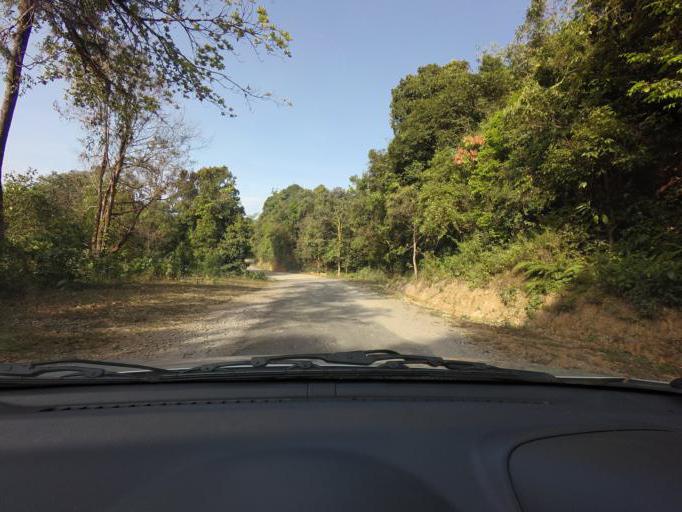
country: IN
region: Karnataka
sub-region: Kodagu
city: Somvarpet
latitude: 12.7126
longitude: 75.6902
